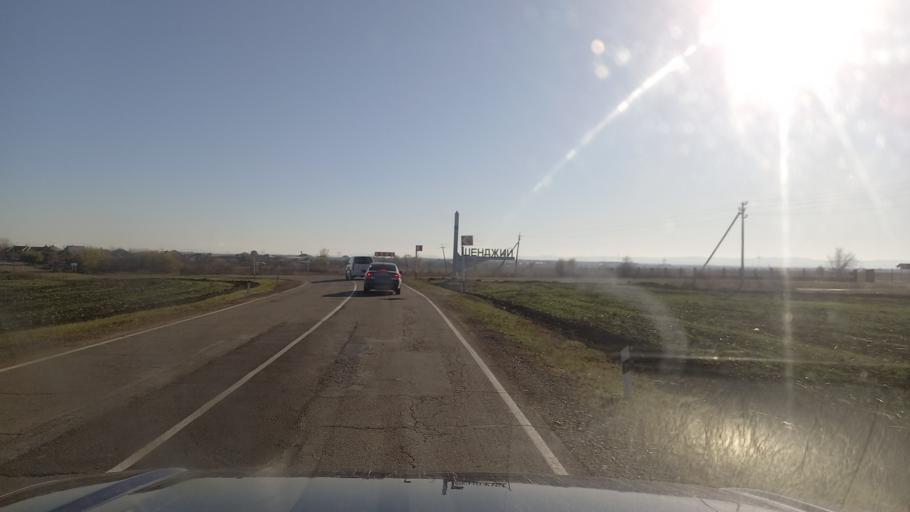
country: RU
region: Adygeya
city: Takhtamukay
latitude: 44.8888
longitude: 39.0551
